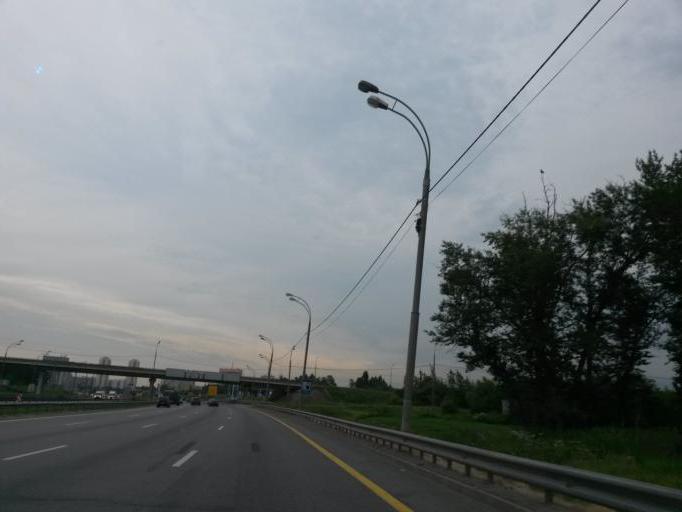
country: RU
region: Moskovskaya
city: Vidnoye
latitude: 55.5678
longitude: 37.6933
